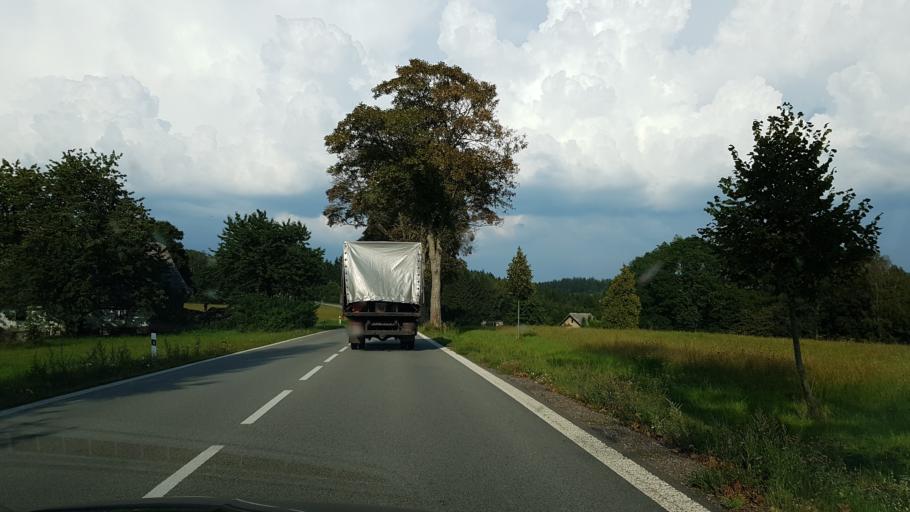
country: CZ
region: Pardubicky
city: Jablonne nad Orlici
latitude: 50.0884
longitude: 16.6020
